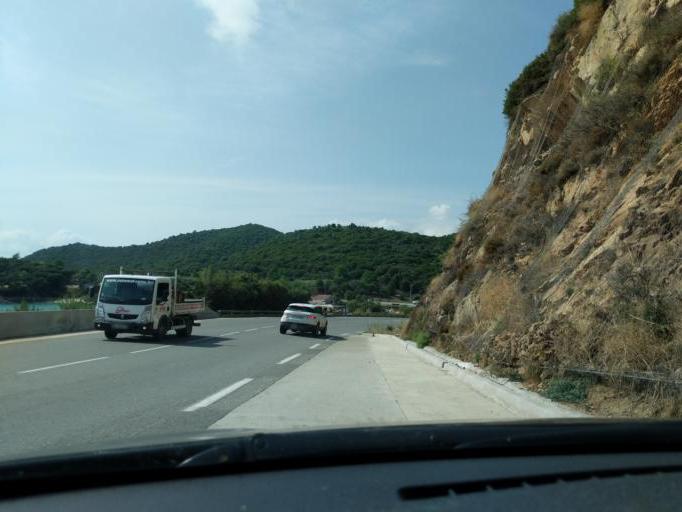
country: FR
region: Corsica
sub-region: Departement de la Corse-du-Sud
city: Sari-Solenzara
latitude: 41.7190
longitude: 9.4021
